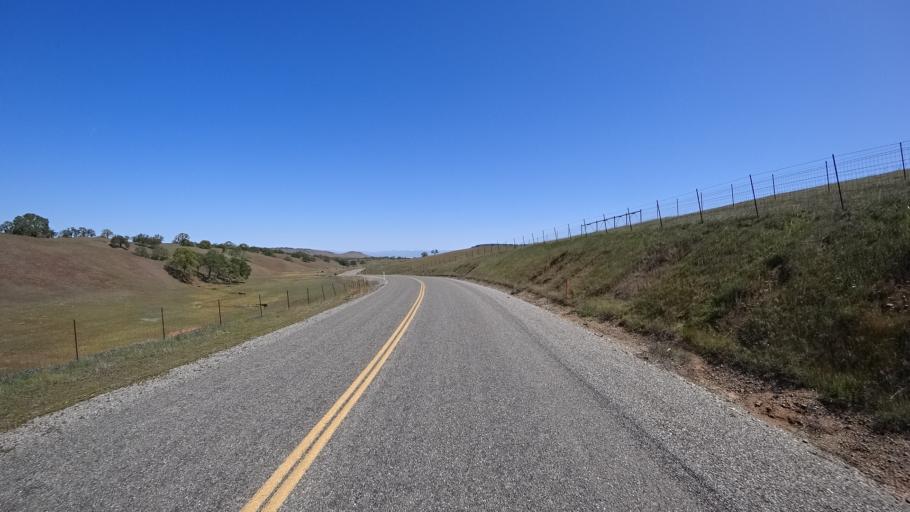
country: US
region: California
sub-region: Glenn County
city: Orland
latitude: 39.7429
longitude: -122.3762
